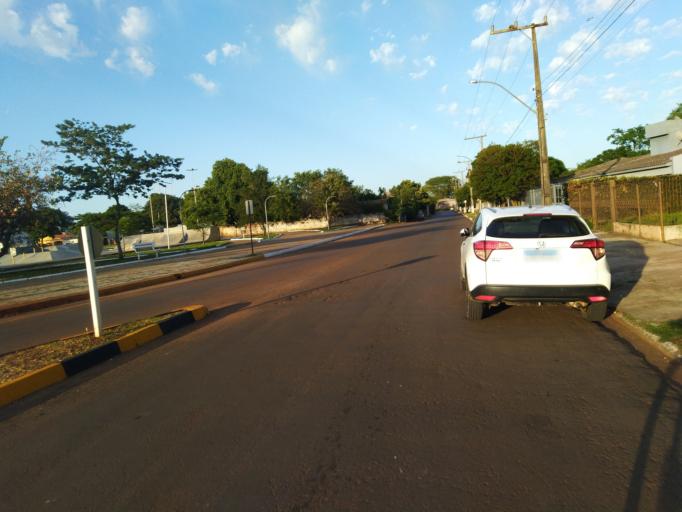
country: BR
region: Rio Grande do Sul
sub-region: Sao Borja
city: Sao Borja
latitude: -28.6501
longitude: -56.0089
